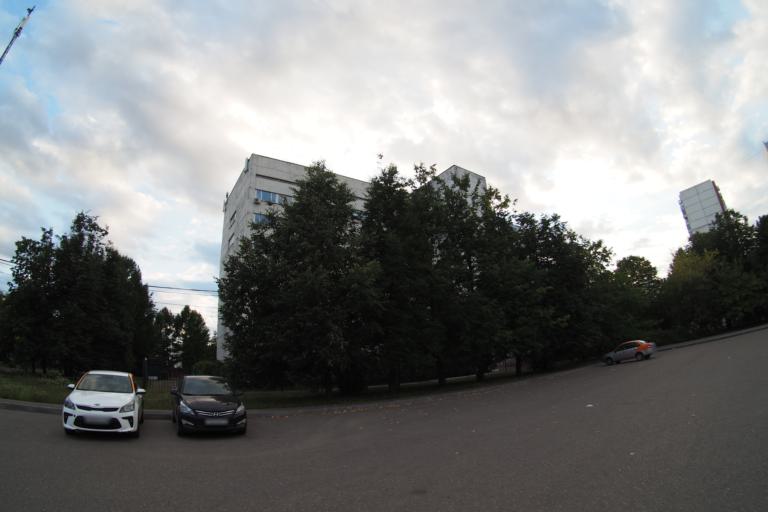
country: RU
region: Moscow
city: Nikulino
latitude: 55.6713
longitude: 37.4652
